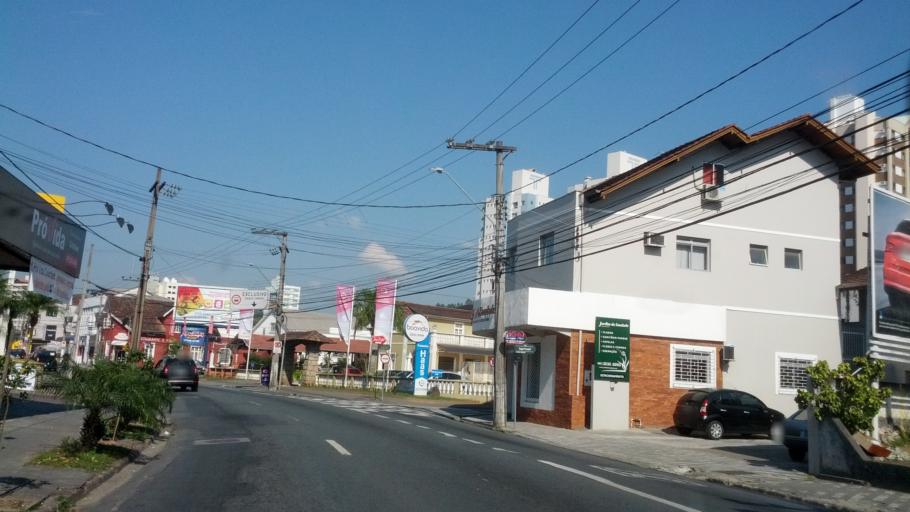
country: BR
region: Santa Catarina
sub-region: Blumenau
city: Blumenau
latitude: -26.9103
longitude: -49.0726
